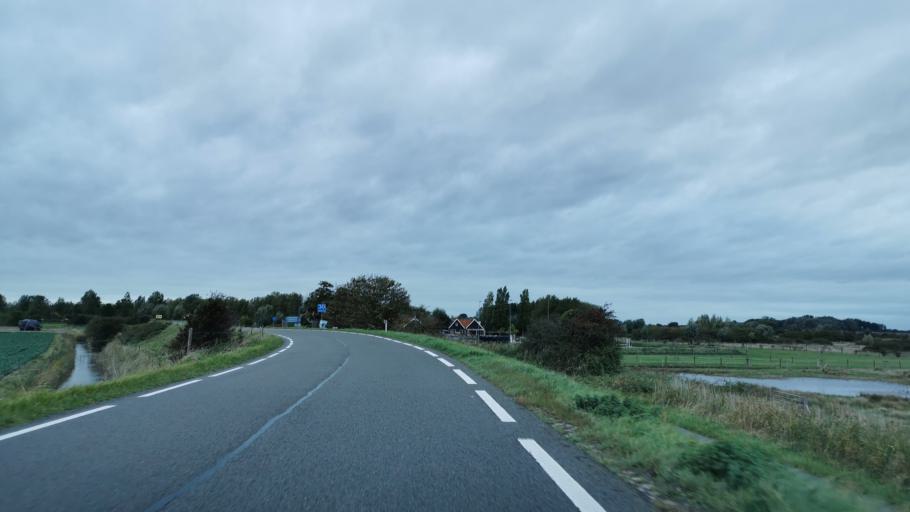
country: NL
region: Zeeland
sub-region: Gemeente Veere
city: Veere
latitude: 51.5643
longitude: 3.6351
